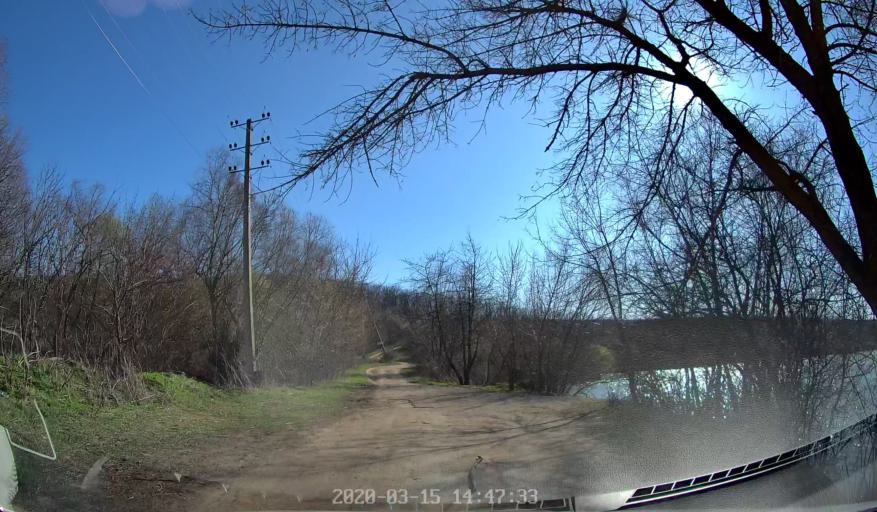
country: MD
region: Orhei
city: Orhei
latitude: 47.2818
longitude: 28.8325
